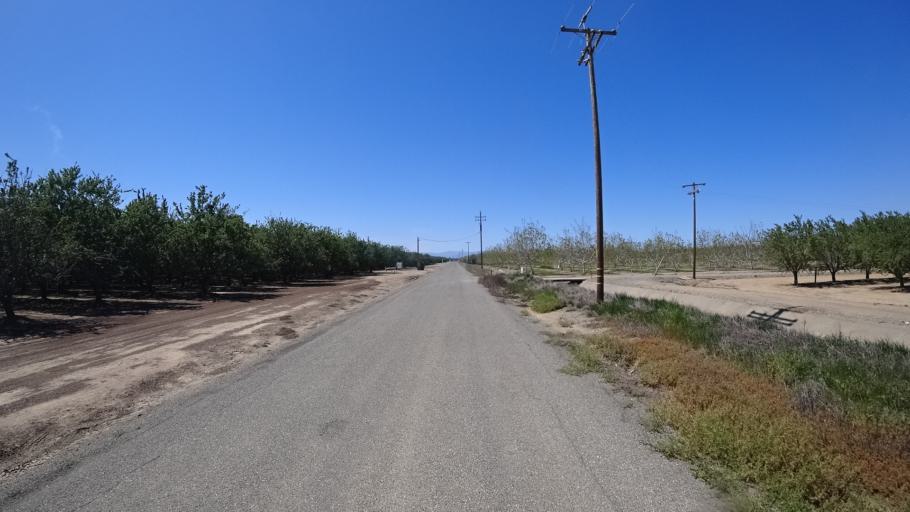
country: US
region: California
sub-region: Glenn County
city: Orland
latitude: 39.7322
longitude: -122.1223
